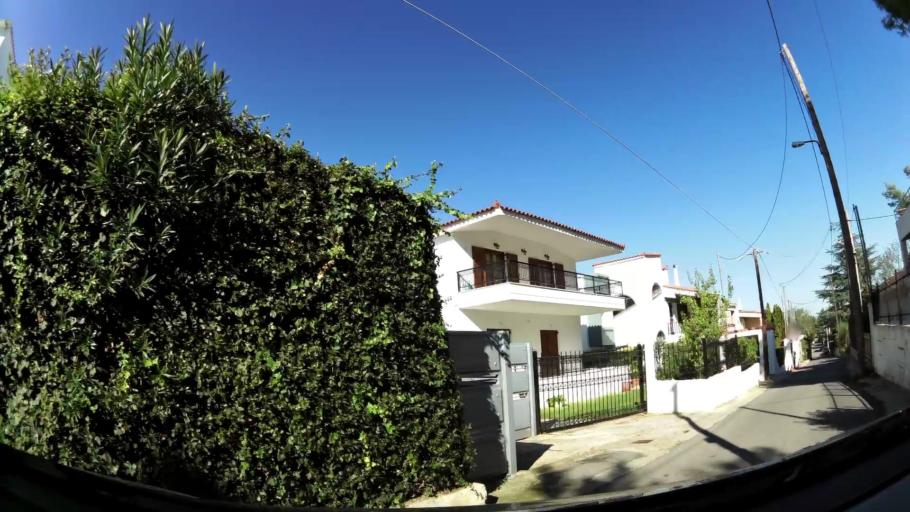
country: GR
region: Attica
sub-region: Nomarchia Anatolikis Attikis
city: Anoixi
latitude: 38.1334
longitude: 23.8630
